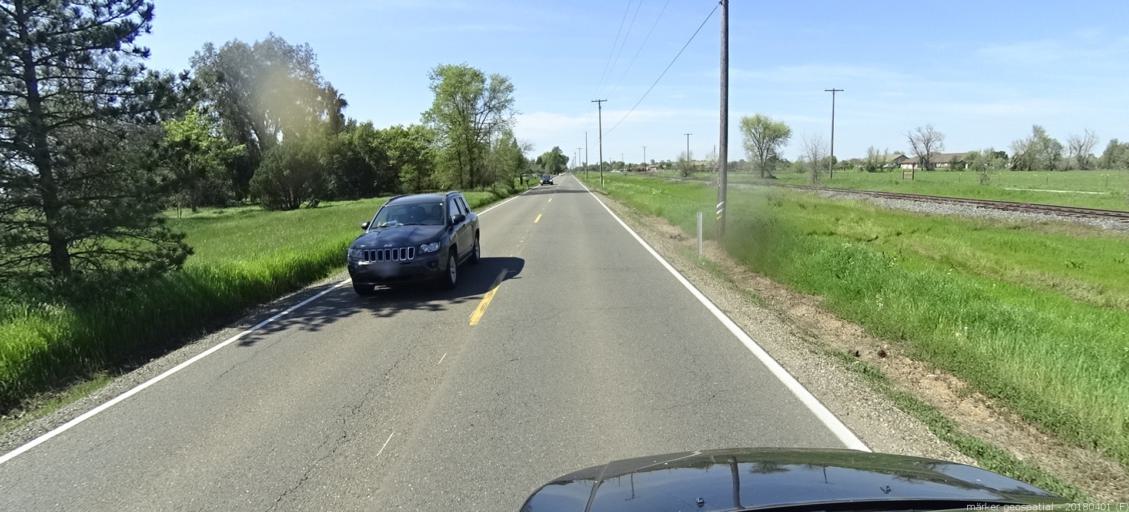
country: US
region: California
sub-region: Sacramento County
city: Wilton
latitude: 38.4041
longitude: -121.2611
